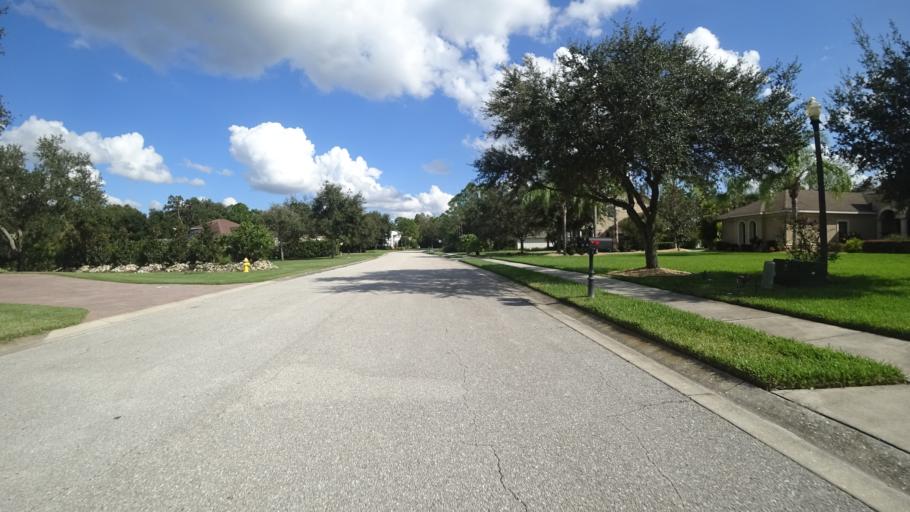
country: US
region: Florida
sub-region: Manatee County
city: Ellenton
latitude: 27.5458
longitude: -82.3822
